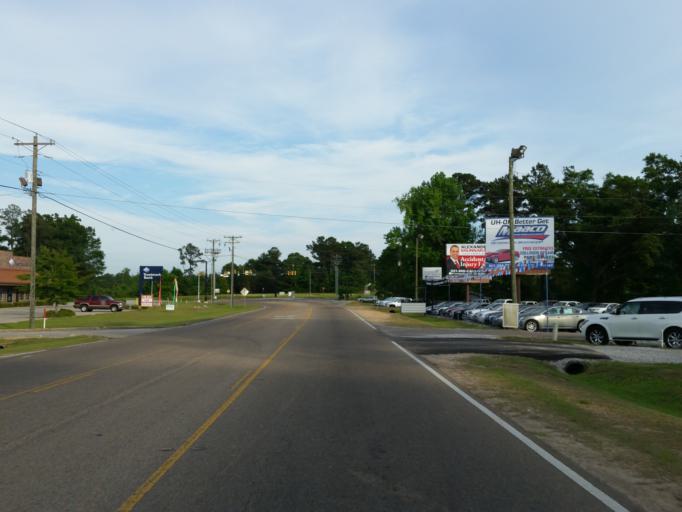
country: US
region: Mississippi
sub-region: Lamar County
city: West Hattiesburg
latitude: 31.3001
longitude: -89.3763
